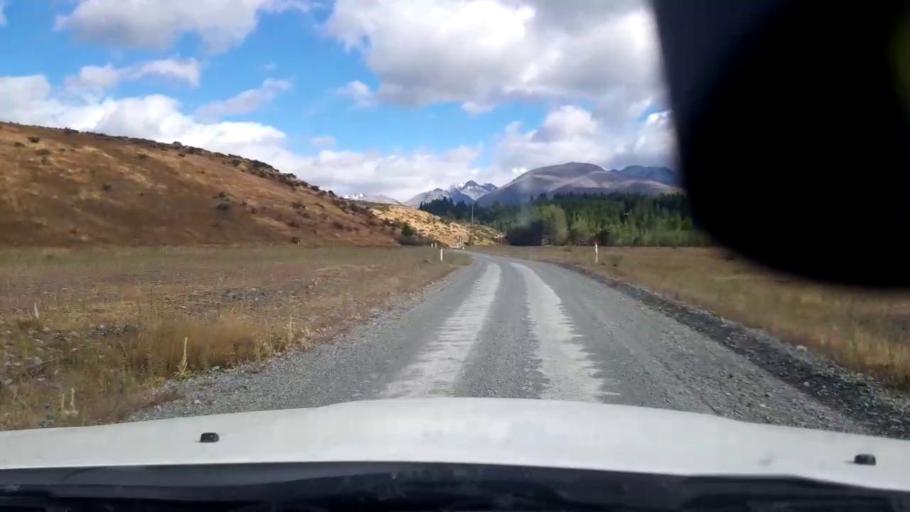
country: NZ
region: Canterbury
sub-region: Timaru District
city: Pleasant Point
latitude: -43.8785
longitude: 170.4663
